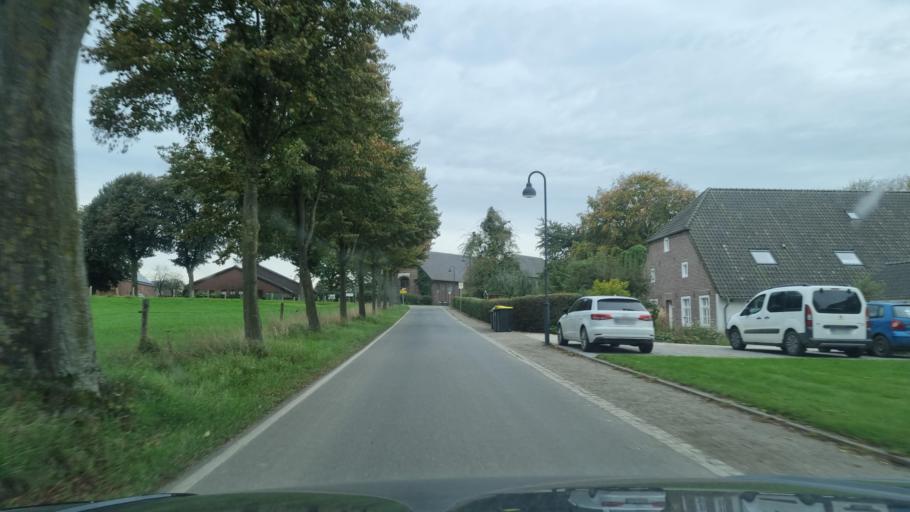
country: DE
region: North Rhine-Westphalia
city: Kalkar
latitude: 51.7279
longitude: 6.2303
